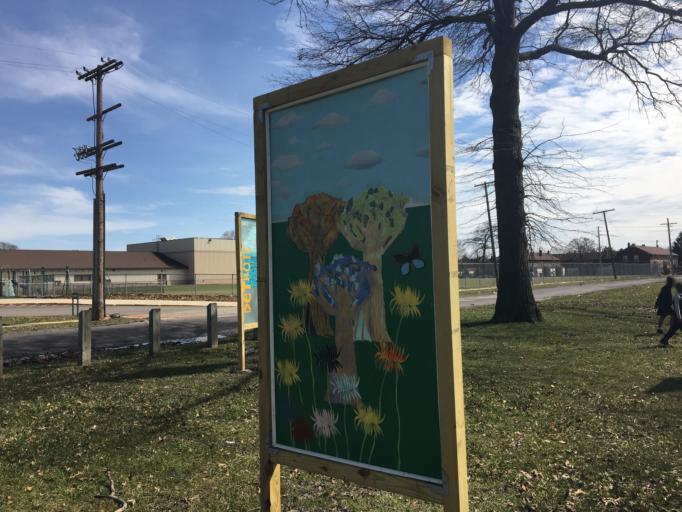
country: US
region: Michigan
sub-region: Wayne County
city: Hamtramck
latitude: 42.4291
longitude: -83.0555
